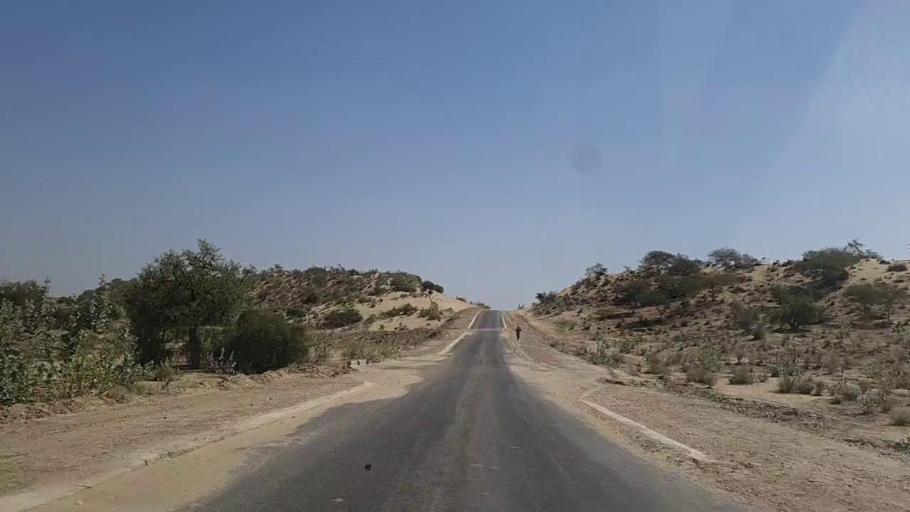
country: PK
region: Sindh
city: Diplo
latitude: 24.4826
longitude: 69.4777
